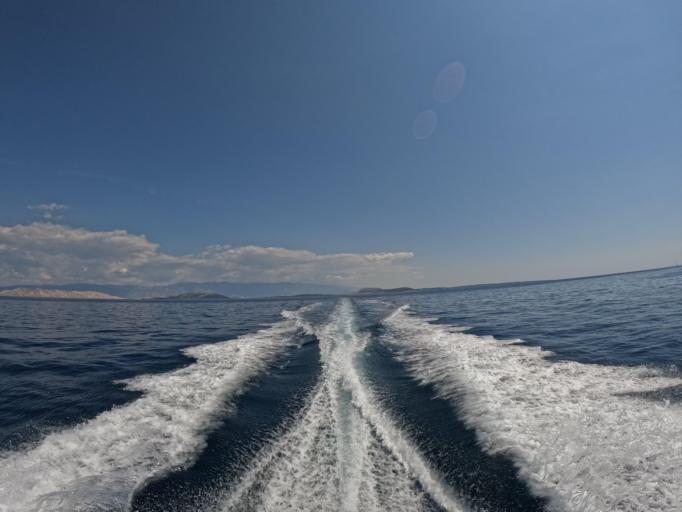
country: HR
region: Primorsko-Goranska
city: Lopar
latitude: 44.8908
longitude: 14.6333
